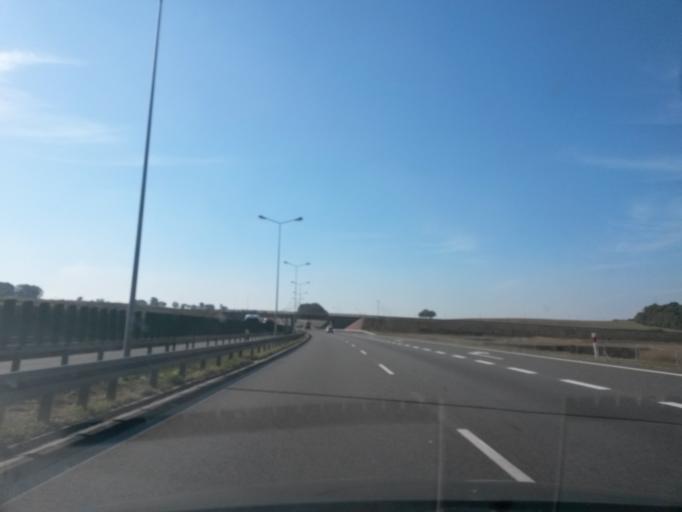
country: PL
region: Opole Voivodeship
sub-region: Powiat strzelecki
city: Strzelce Opolskie
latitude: 50.4592
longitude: 18.2765
